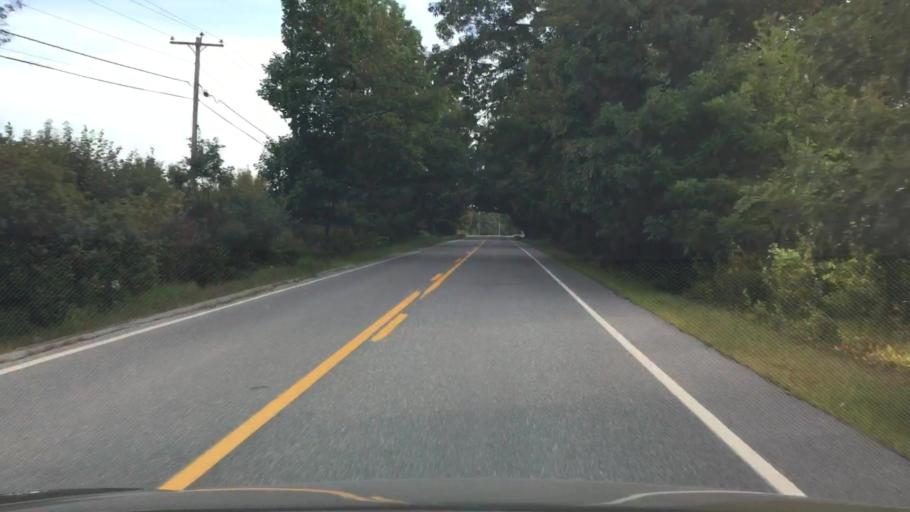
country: US
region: Maine
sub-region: Hancock County
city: Castine
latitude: 44.4394
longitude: -68.7902
